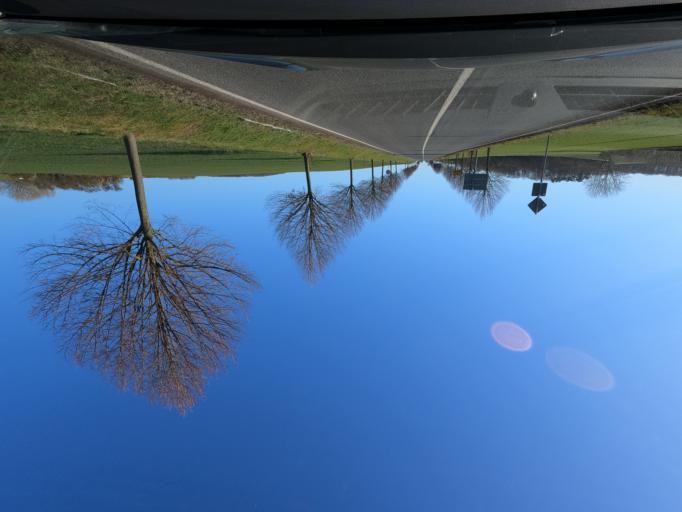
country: DE
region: Saxony-Anhalt
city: Wasserleben
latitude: 51.9846
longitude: 10.7784
